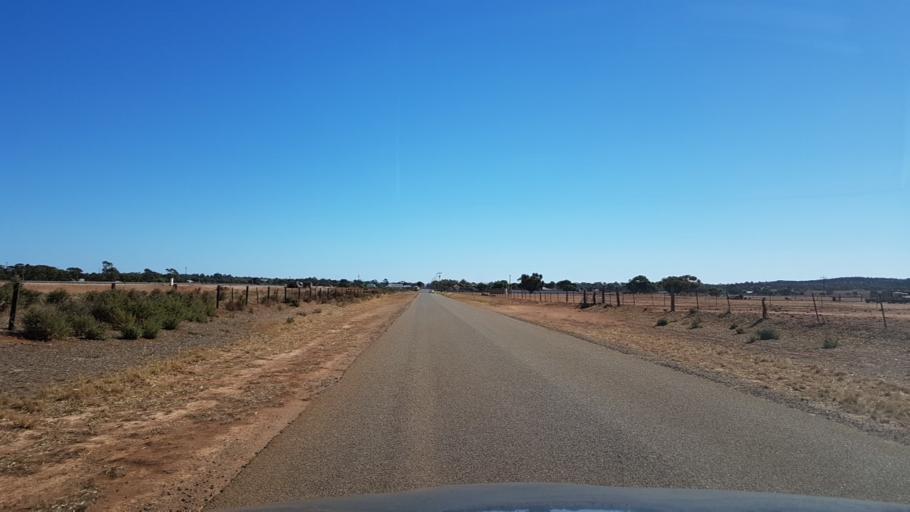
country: AU
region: South Australia
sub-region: Peterborough
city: Peterborough
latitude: -32.9714
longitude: 138.8576
